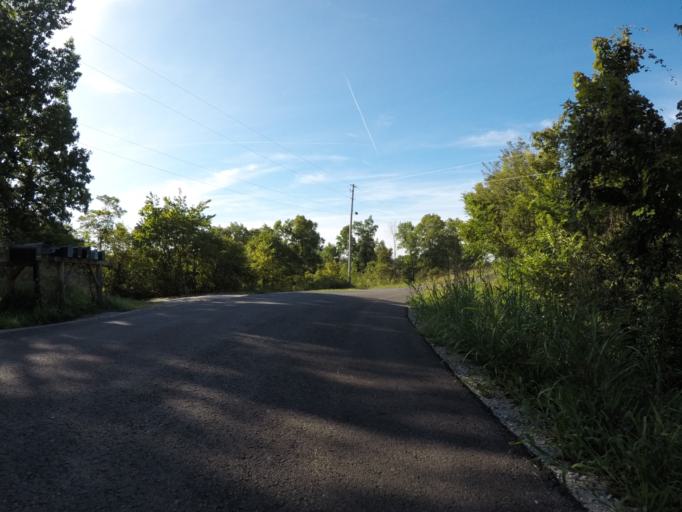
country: US
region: Ohio
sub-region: Lawrence County
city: Burlington
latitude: 38.5235
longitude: -82.5241
